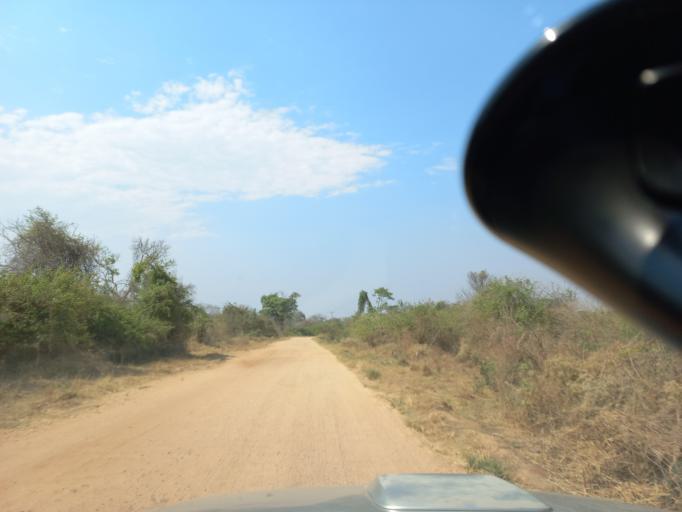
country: ZW
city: Chirundu
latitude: -15.9274
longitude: 28.8730
